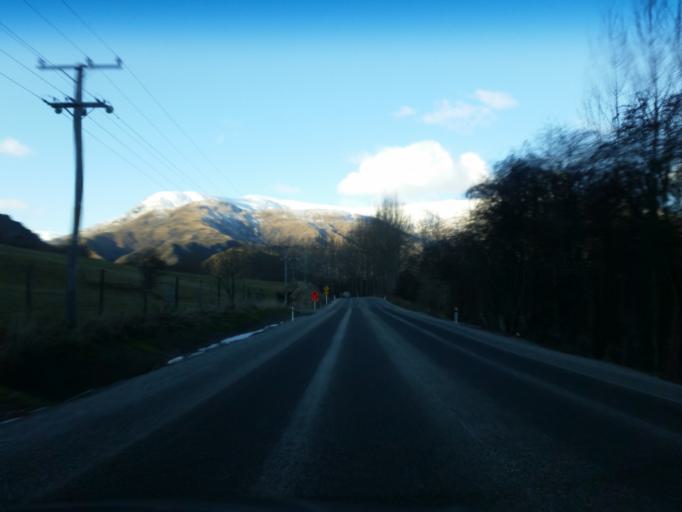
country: NZ
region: Otago
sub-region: Queenstown-Lakes District
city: Arrowtown
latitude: -44.9453
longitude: 168.8017
